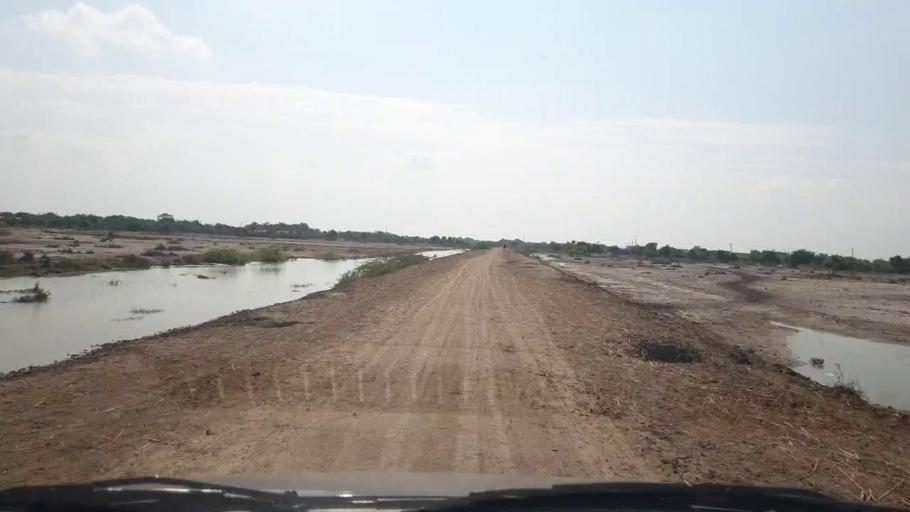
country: PK
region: Sindh
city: Badin
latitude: 24.4828
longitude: 68.6123
